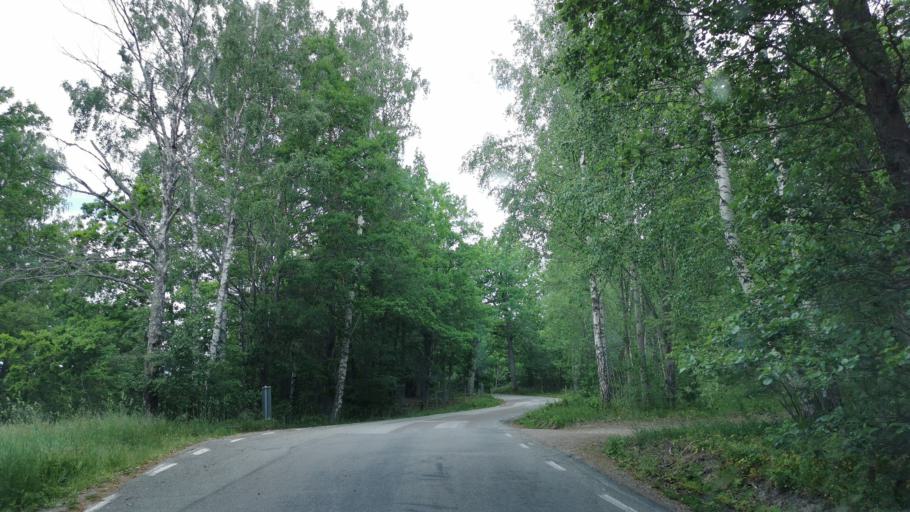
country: SE
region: Vaestra Goetaland
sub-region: Bengtsfors Kommun
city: Dals Langed
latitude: 58.8435
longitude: 12.4098
